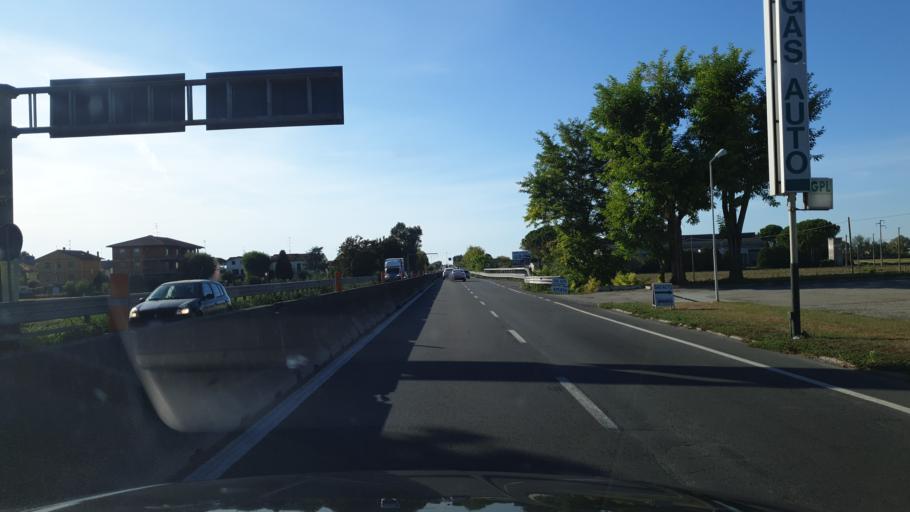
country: IT
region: Emilia-Romagna
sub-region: Provincia di Ravenna
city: Madonna Dell'Albero
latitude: 44.3808
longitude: 12.2059
